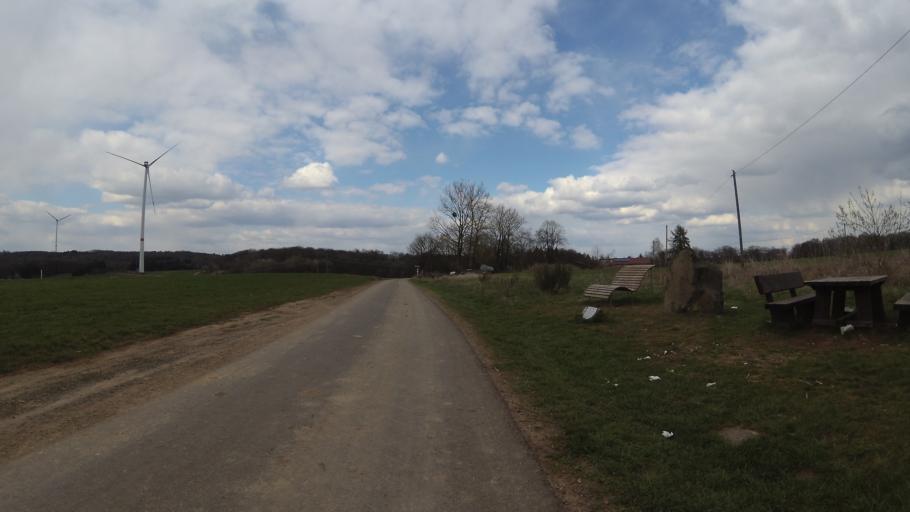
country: DE
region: Saarland
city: Marpingen
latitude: 49.4785
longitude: 7.0866
